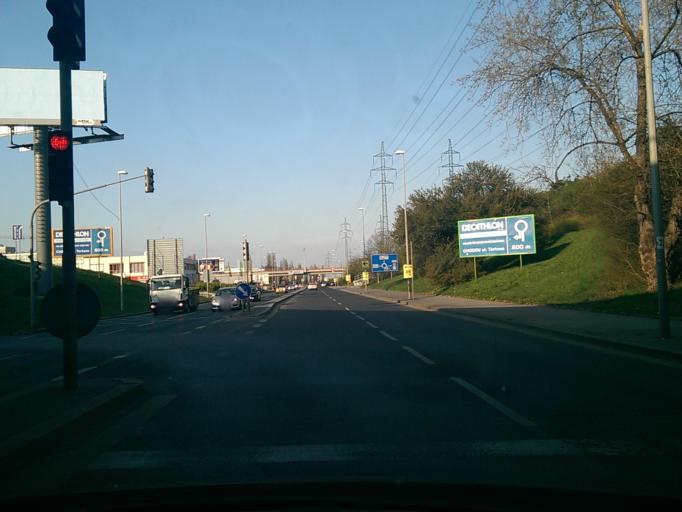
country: CZ
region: Central Bohemia
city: Vestec
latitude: 50.0345
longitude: 14.4923
